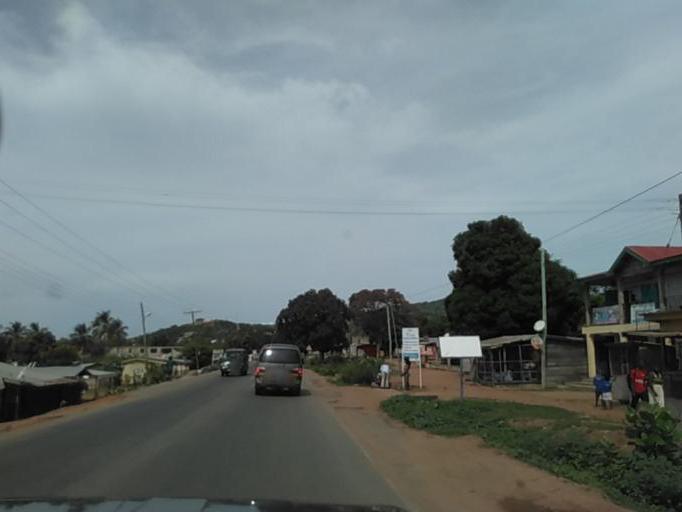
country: GH
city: Akropong
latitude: 6.2298
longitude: 0.0904
